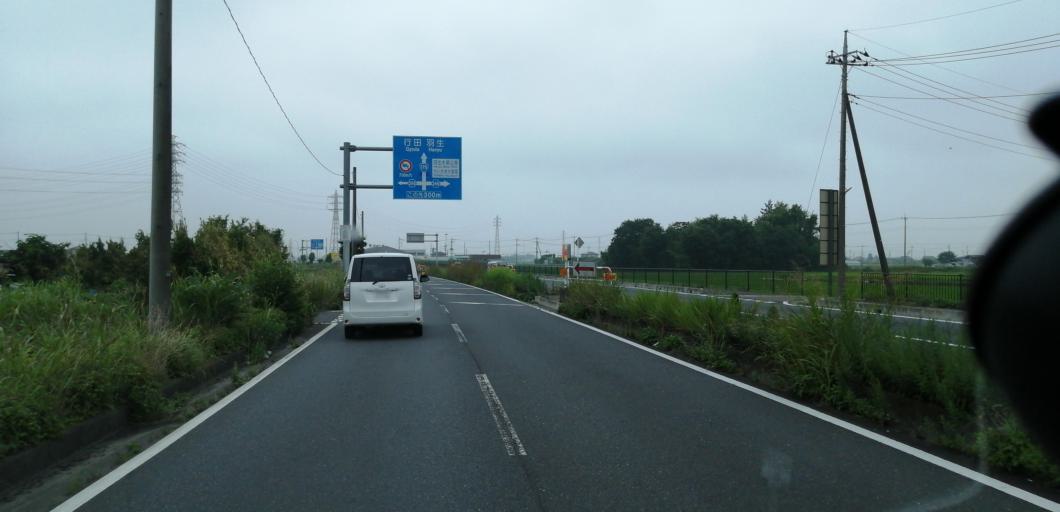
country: JP
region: Saitama
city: Kazo
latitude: 36.1394
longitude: 139.5934
